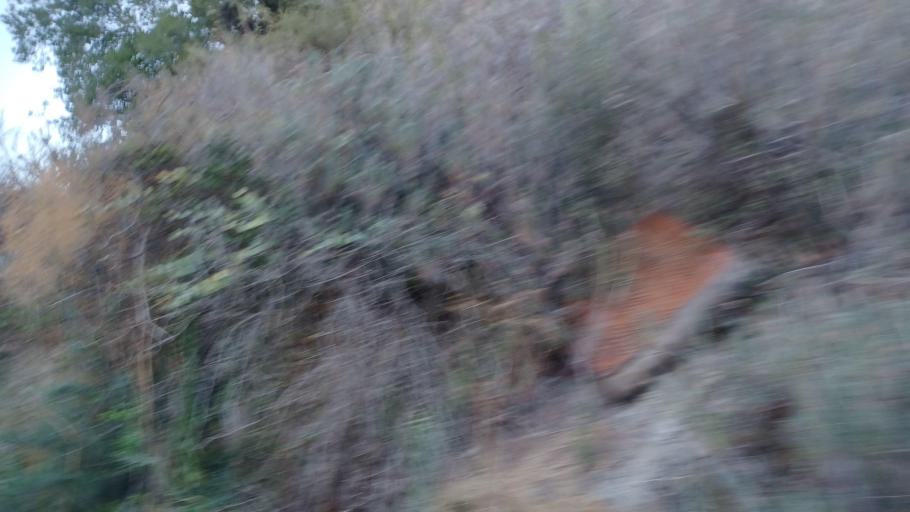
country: CY
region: Pafos
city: Polis
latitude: 34.9831
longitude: 32.4630
